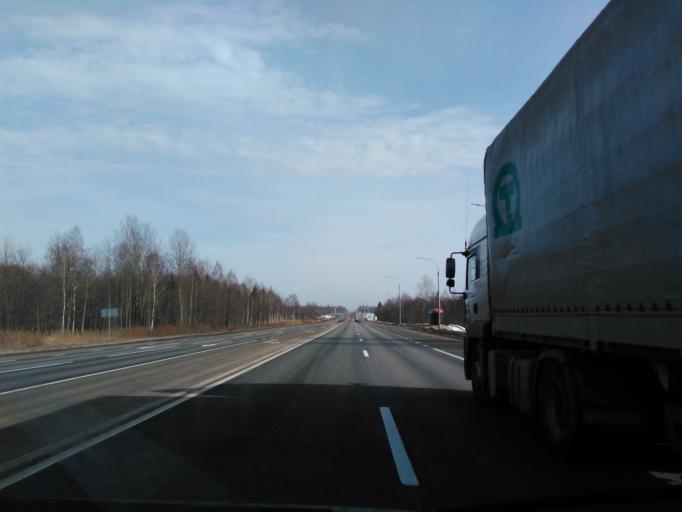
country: BY
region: Vitebsk
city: Dubrowna
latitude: 54.6900
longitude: 30.9322
